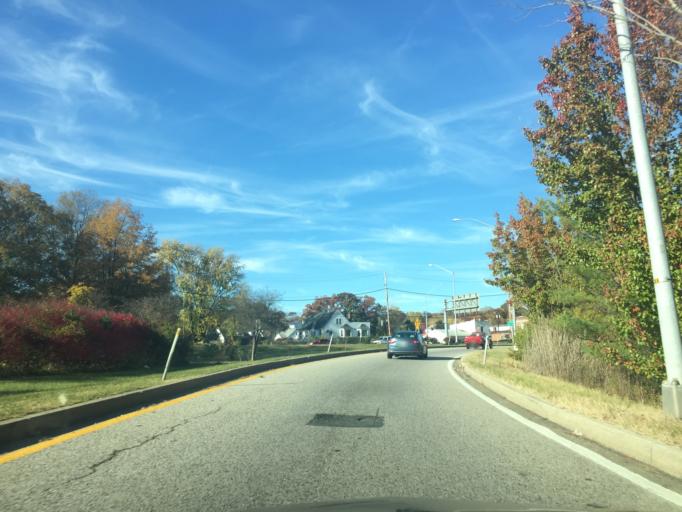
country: US
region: Maryland
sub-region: Baltimore County
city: Overlea
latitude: 39.3702
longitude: -76.5119
